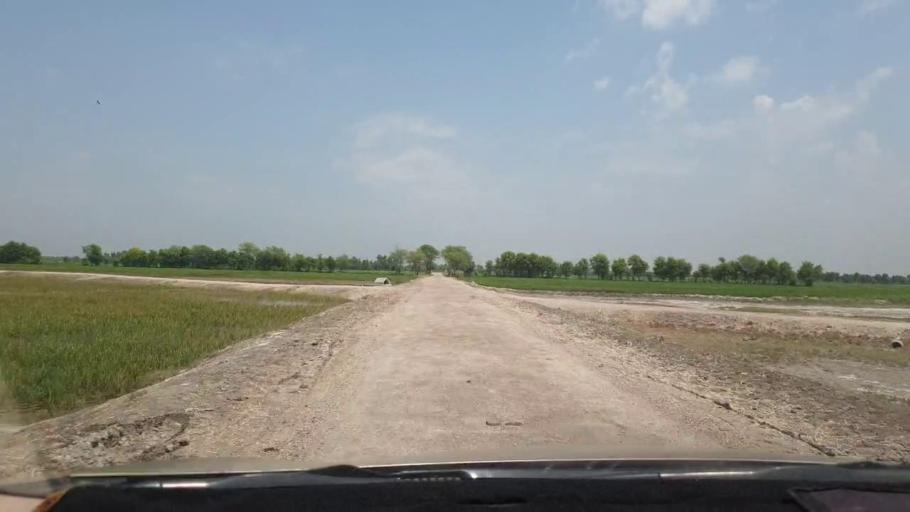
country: PK
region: Sindh
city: Naudero
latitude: 27.7373
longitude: 68.3570
